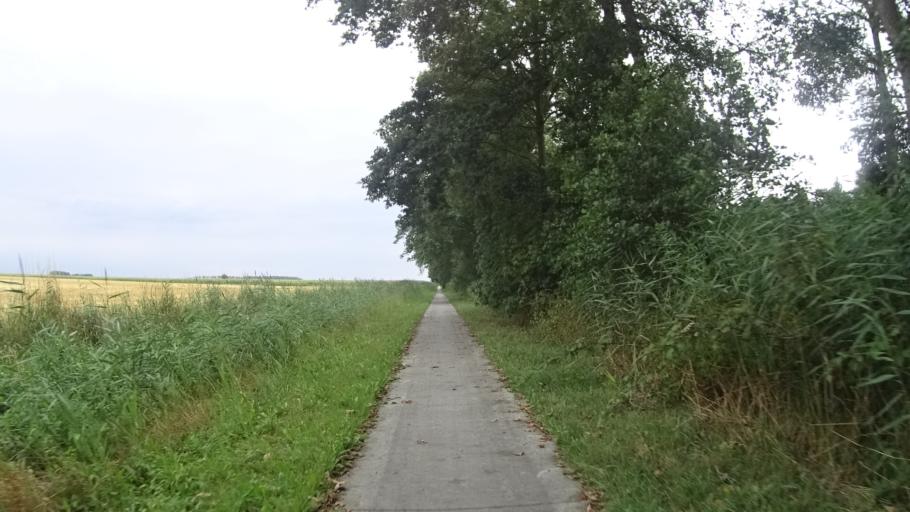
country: NL
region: Groningen
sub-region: Gemeente Slochteren
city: Slochteren
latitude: 53.2142
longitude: 6.8167
